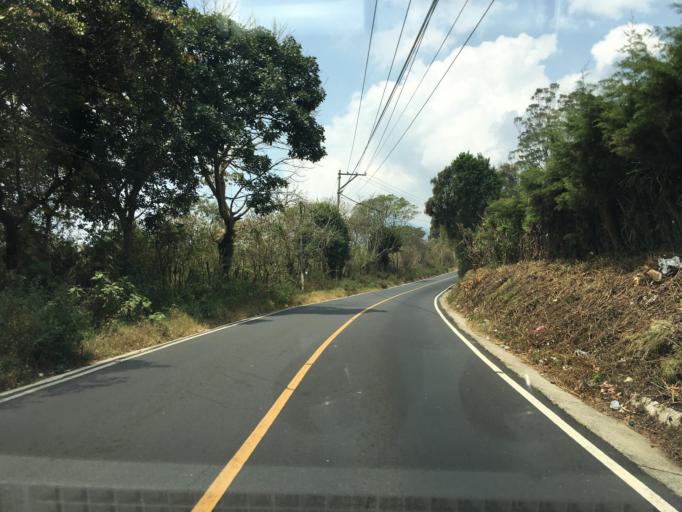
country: GT
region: Guatemala
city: Villa Canales
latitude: 14.4085
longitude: -90.5376
